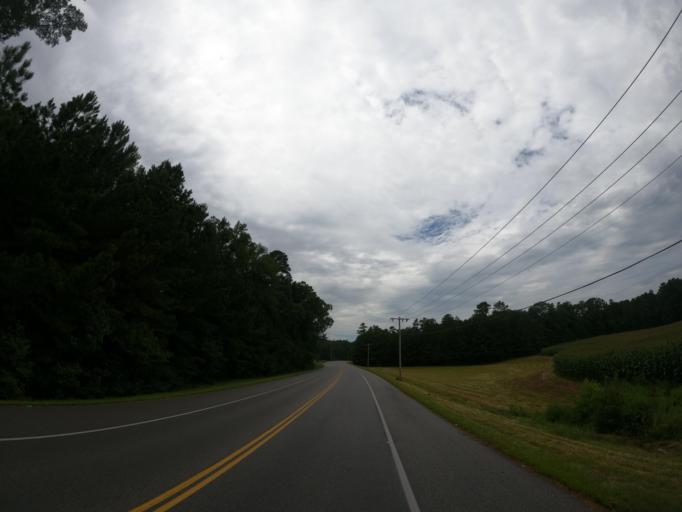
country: US
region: Maryland
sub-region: Saint Mary's County
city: California
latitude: 38.2782
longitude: -76.5480
